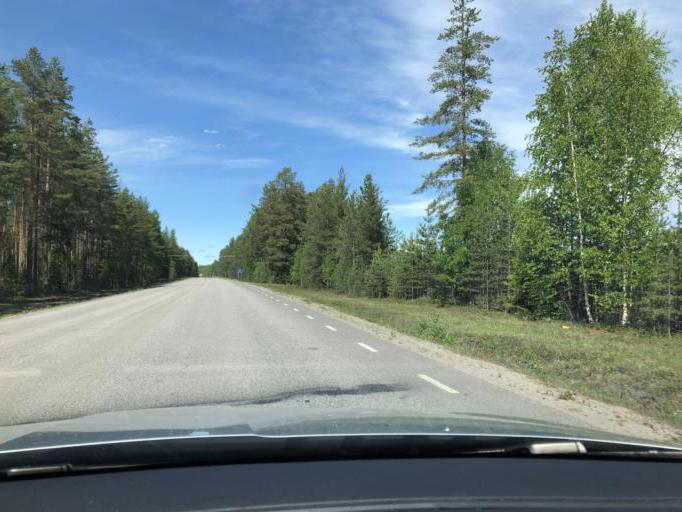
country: SE
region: Norrbotten
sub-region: Pitea Kommun
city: Bergsviken
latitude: 65.3755
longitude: 21.3489
